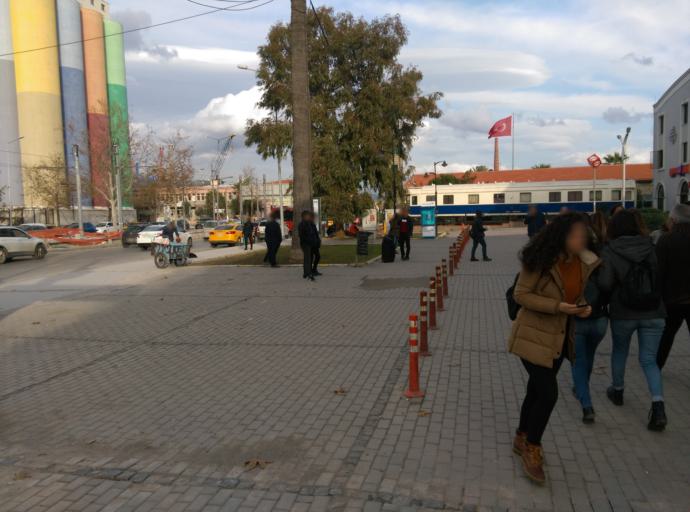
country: TR
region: Izmir
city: Izmir
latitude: 38.4393
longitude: 27.1479
